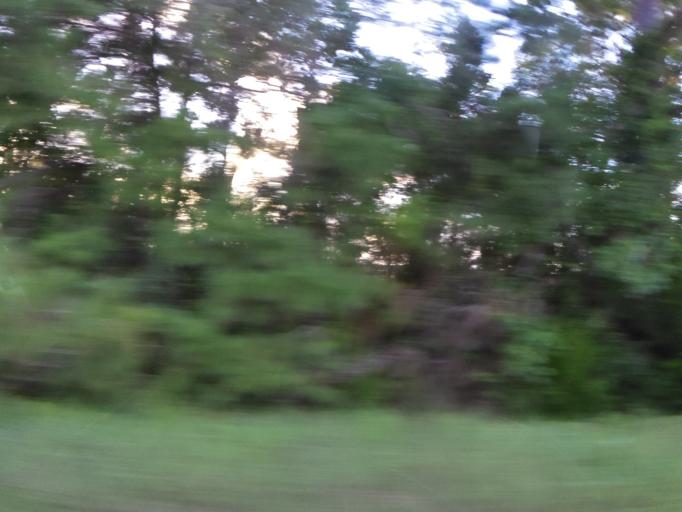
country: US
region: Georgia
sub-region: Glynn County
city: Brunswick
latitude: 31.1106
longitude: -81.6170
